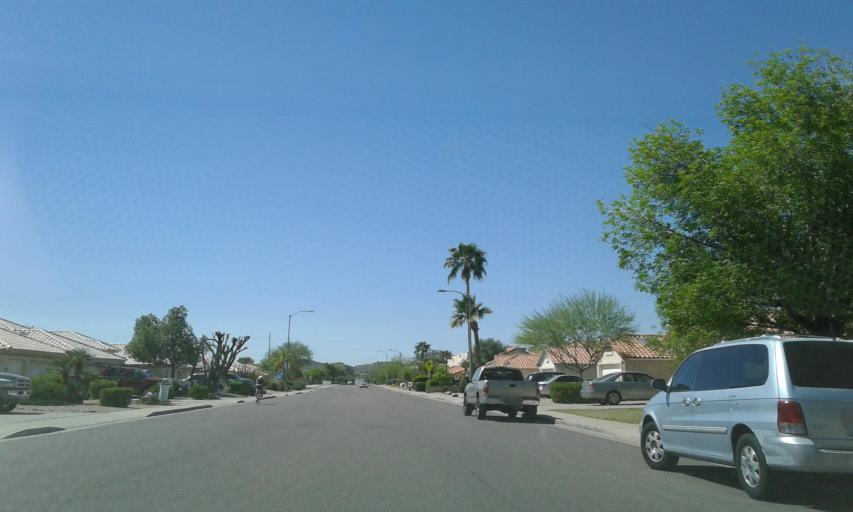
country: US
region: Arizona
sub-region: Maricopa County
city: Paradise Valley
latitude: 33.6625
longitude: -112.0073
